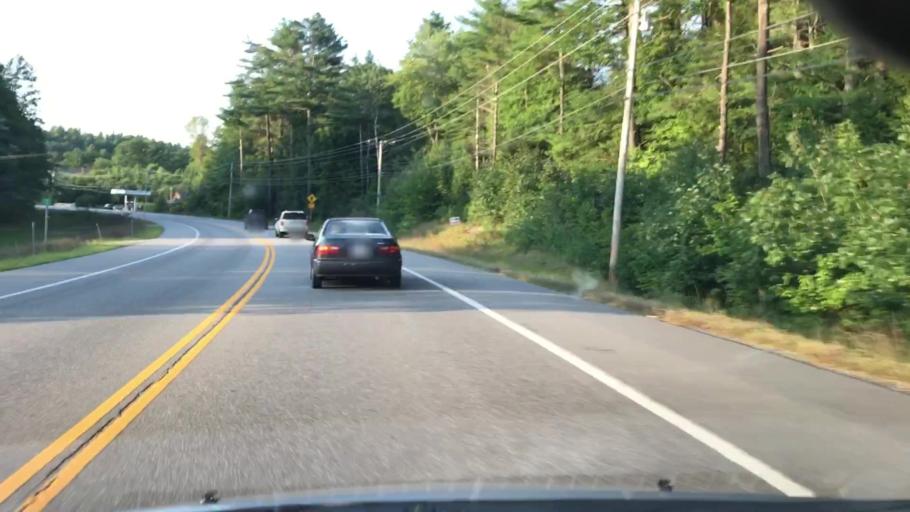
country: US
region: New Hampshire
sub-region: Grafton County
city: Rumney
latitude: 43.8638
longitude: -71.9102
